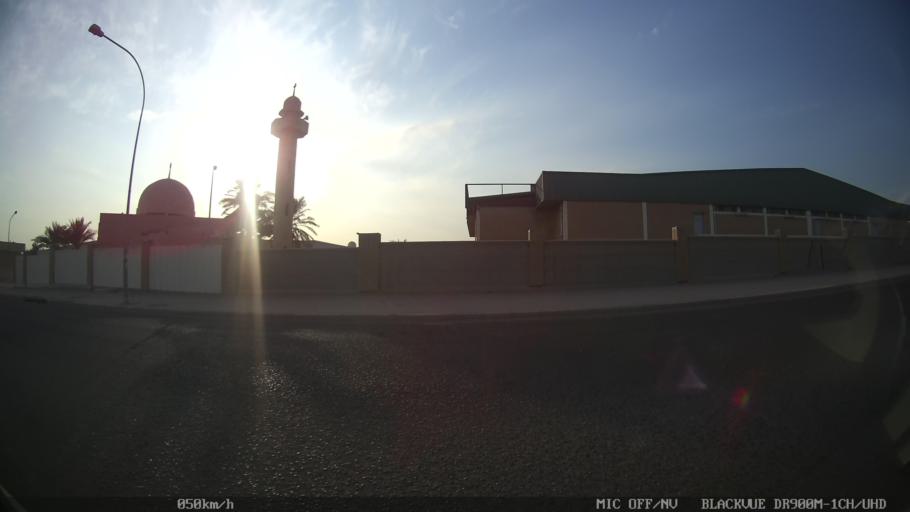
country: KW
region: Al Farwaniyah
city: Janub as Surrah
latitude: 29.2364
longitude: 48.0094
